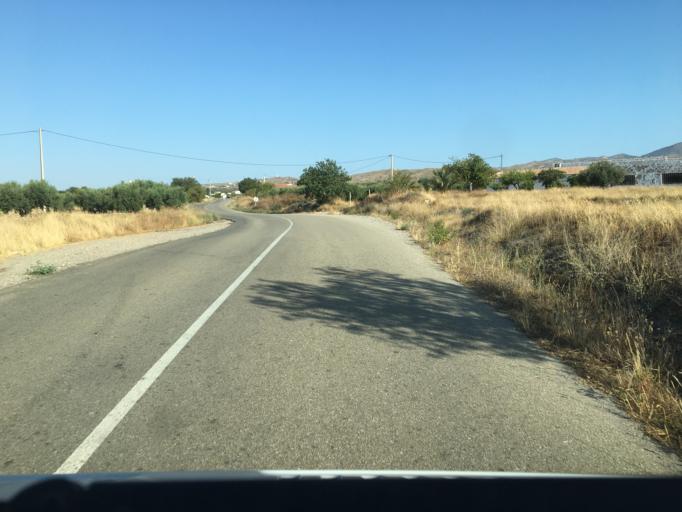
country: ES
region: Andalusia
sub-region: Provincia de Almeria
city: Huercal-Overa
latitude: 37.4668
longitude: -1.8860
